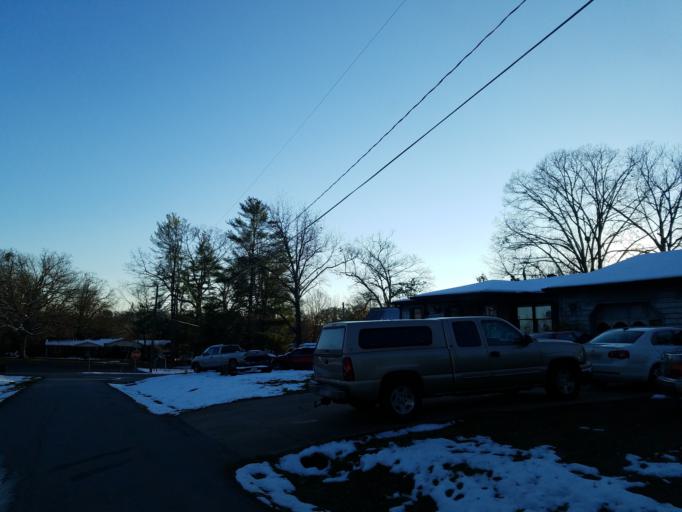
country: US
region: Georgia
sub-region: Dawson County
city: Dawsonville
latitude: 34.4197
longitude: -84.1204
